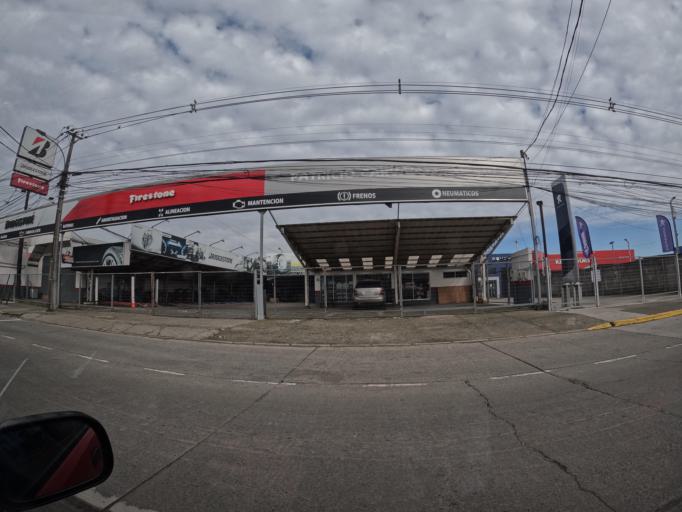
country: CL
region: Maule
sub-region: Provincia de Linares
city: Linares
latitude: -35.8448
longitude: -71.6042
